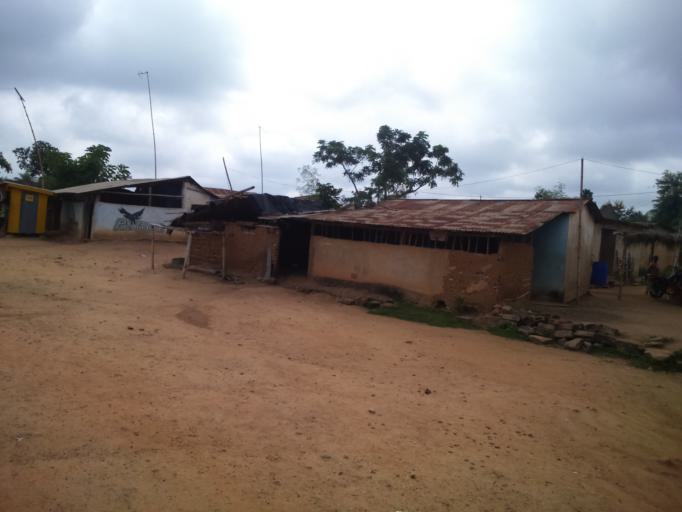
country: CI
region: Agneby
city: Agboville
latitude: 6.0275
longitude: -4.1315
